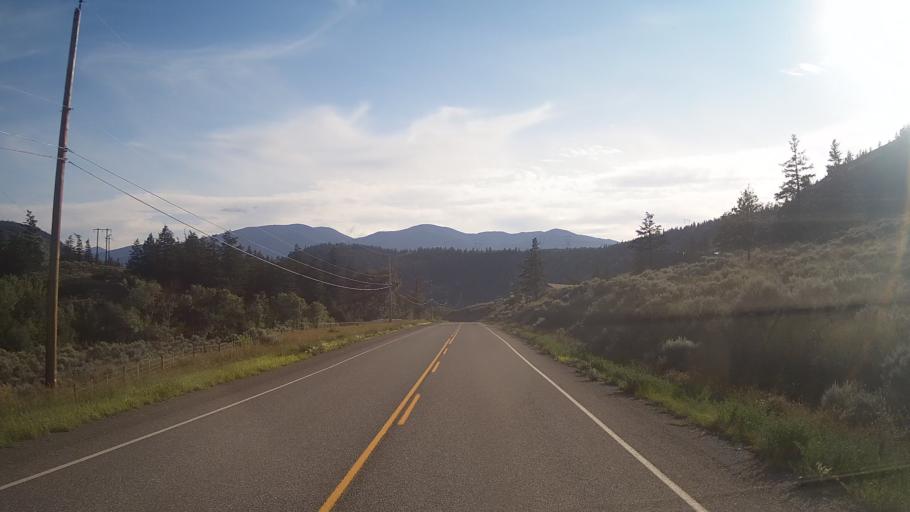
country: CA
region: British Columbia
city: Lillooet
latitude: 50.8865
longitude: -121.8153
